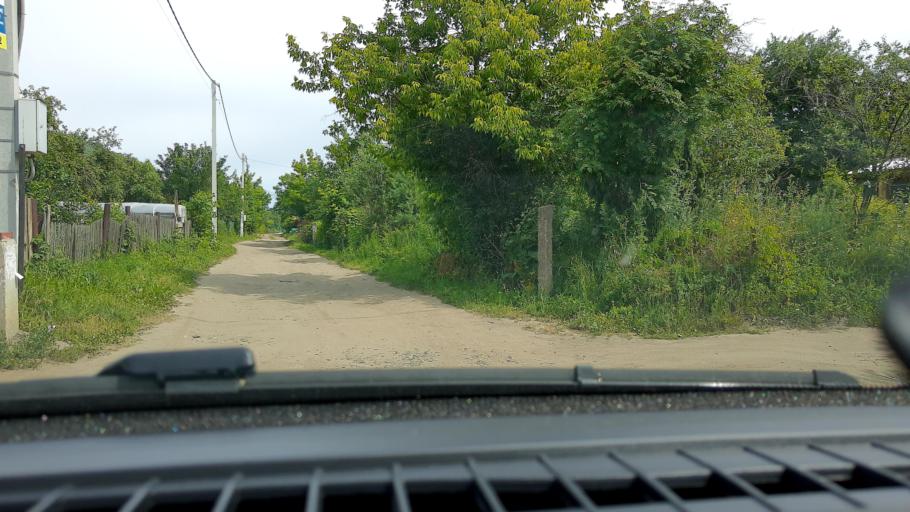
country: RU
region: Nizjnij Novgorod
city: Nizhniy Novgorod
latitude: 56.2681
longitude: 43.9548
